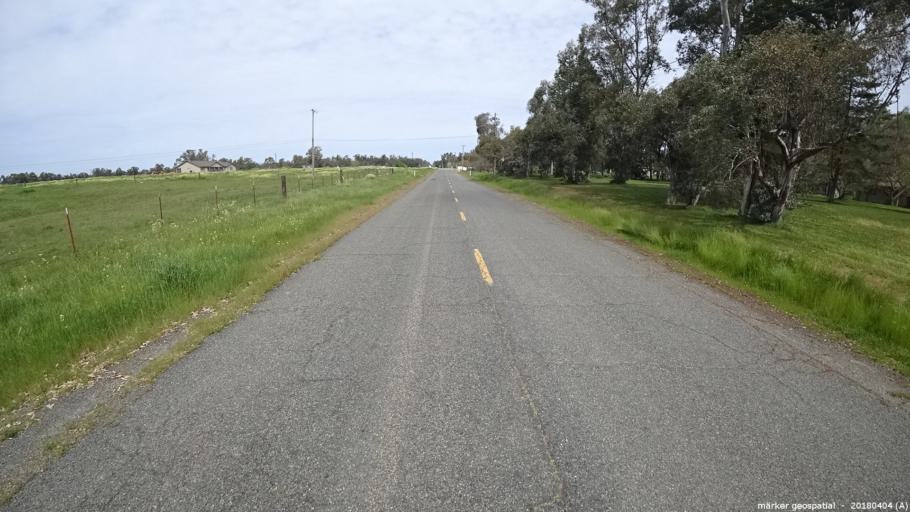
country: US
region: California
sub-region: Sacramento County
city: Clay
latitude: 38.3155
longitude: -121.1449
